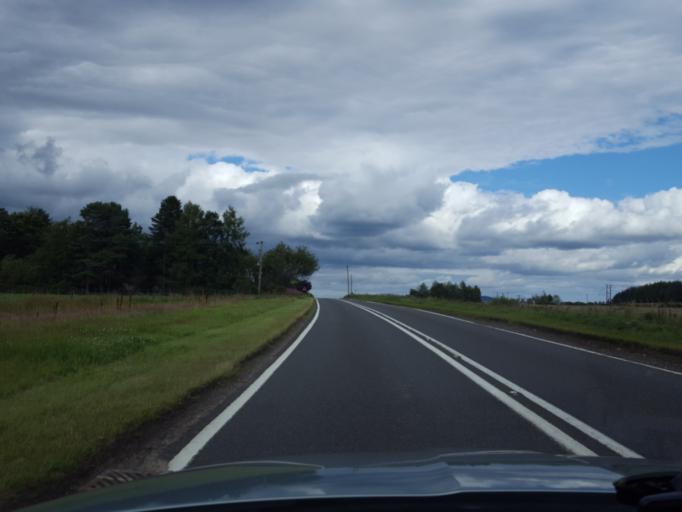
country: GB
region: Scotland
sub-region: Moray
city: Rothes
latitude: 57.4499
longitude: -3.2584
